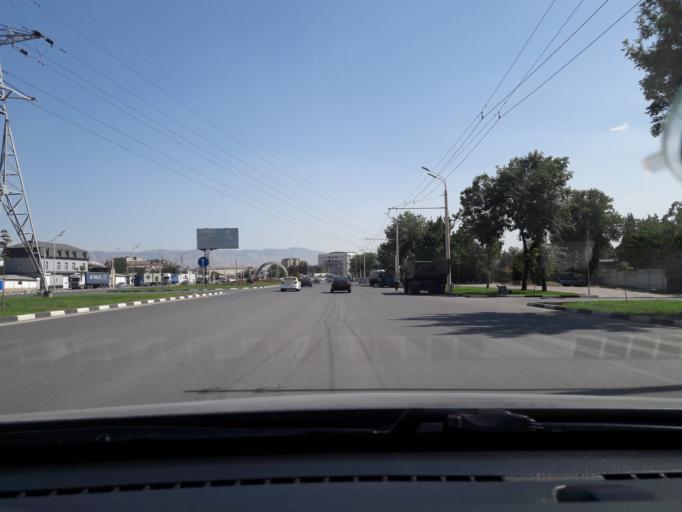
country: TJ
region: Dushanbe
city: Dushanbe
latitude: 38.5399
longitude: 68.7409
